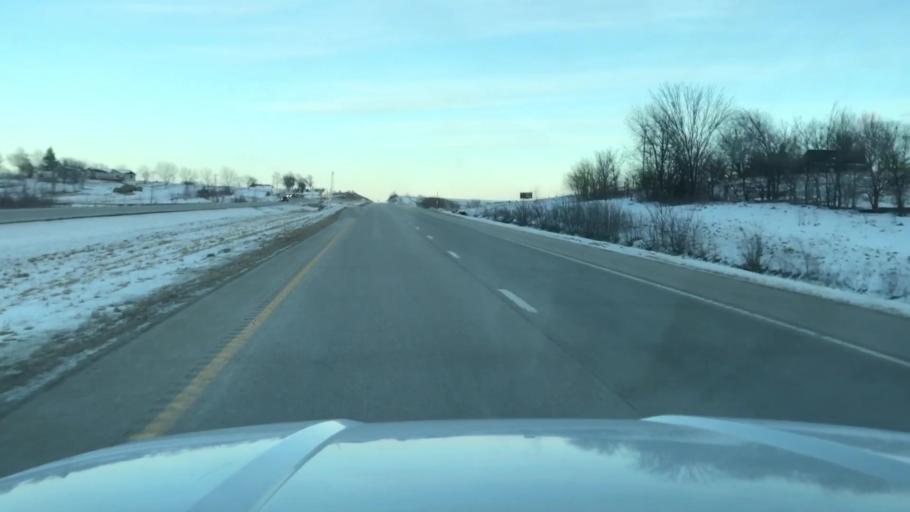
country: US
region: Missouri
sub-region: Clinton County
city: Gower
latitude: 39.7612
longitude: -94.5558
